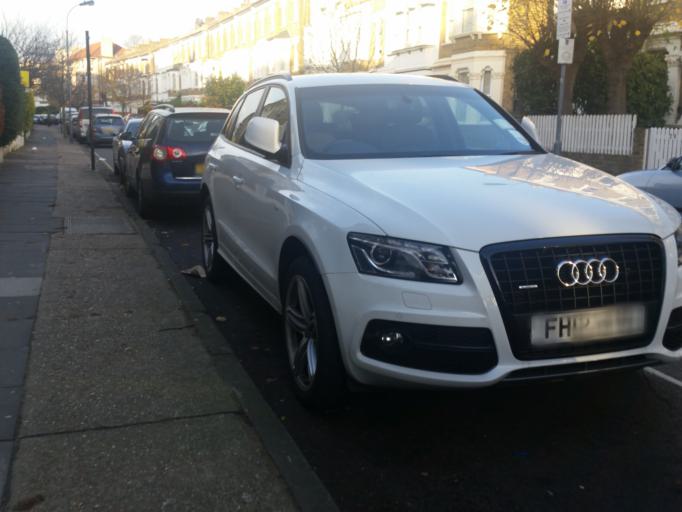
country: GB
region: England
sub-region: Greater London
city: Hammersmith
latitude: 51.5065
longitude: -0.2270
